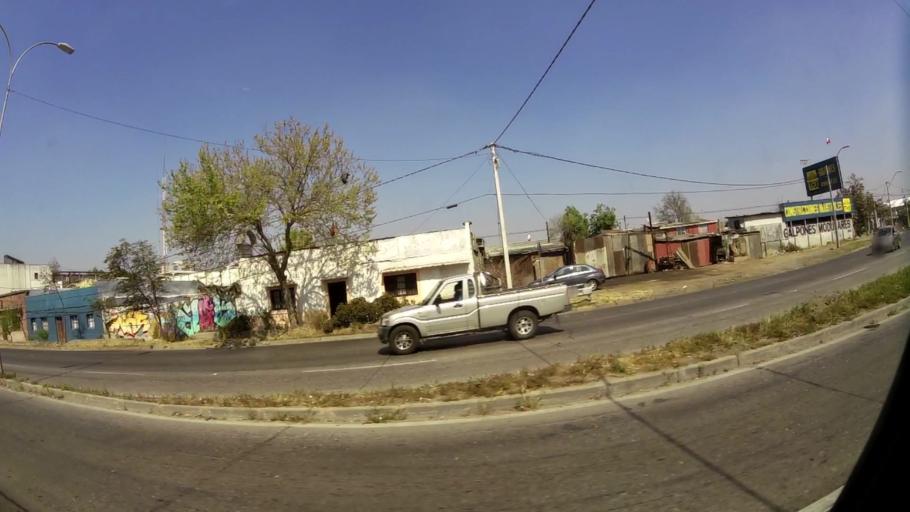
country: CL
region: Santiago Metropolitan
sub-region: Provincia de Santiago
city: Santiago
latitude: -33.4773
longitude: -70.6576
